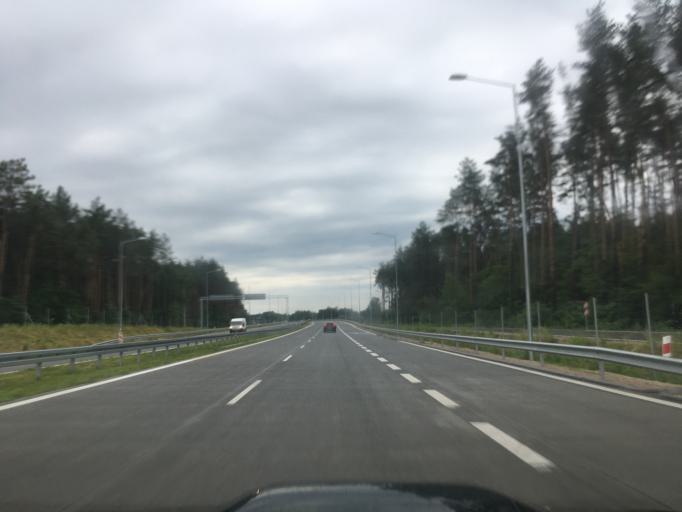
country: PL
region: Masovian Voivodeship
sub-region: Powiat piaseczynski
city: Gora Kalwaria
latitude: 51.9735
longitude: 21.1919
